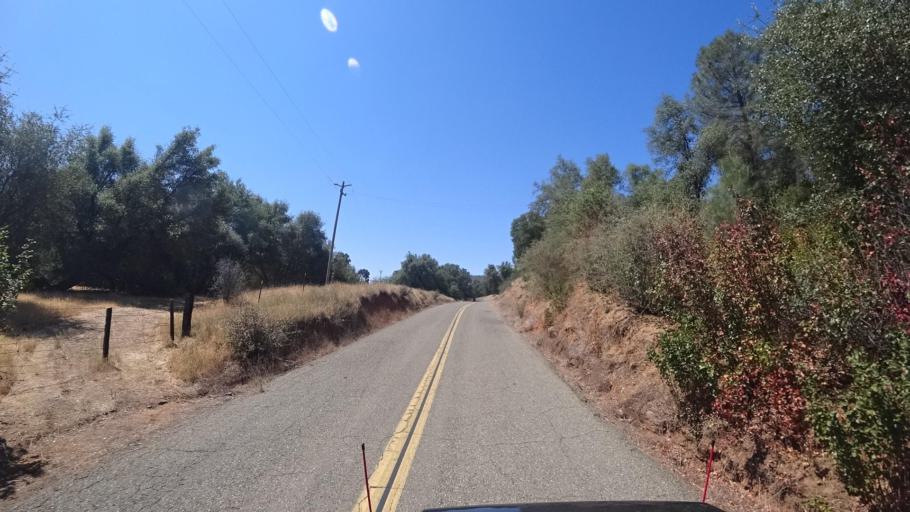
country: US
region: California
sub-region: Mariposa County
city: Mariposa
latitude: 37.3987
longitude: -119.9672
